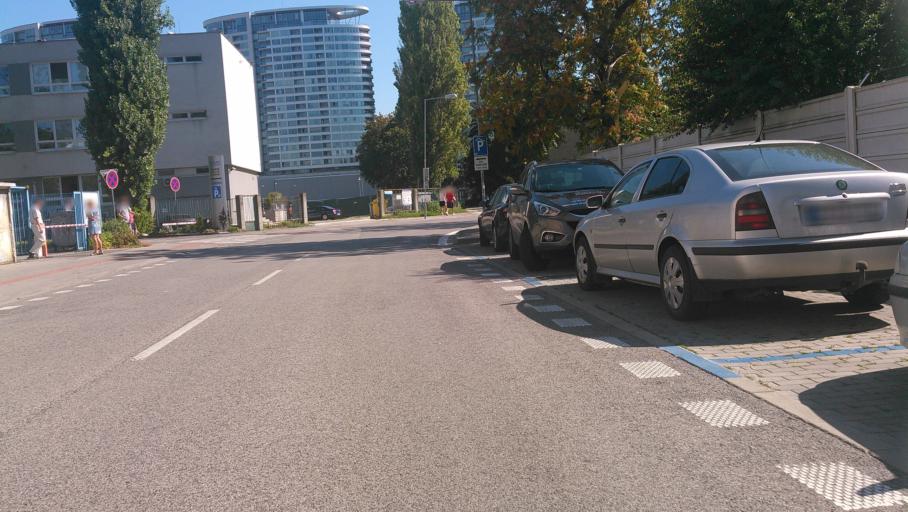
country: SK
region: Bratislavsky
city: Bratislava
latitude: 48.1616
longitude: 17.1362
